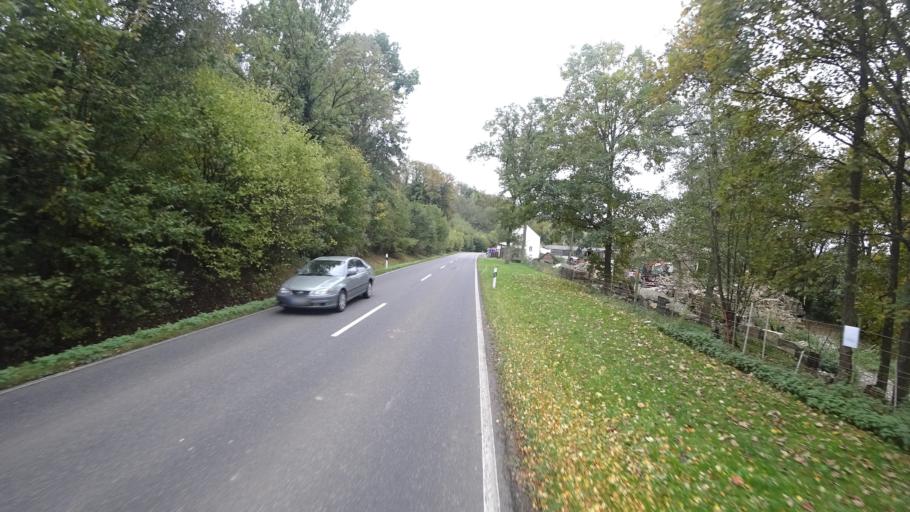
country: DE
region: Rheinland-Pfalz
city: Selters
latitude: 50.5265
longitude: 7.7483
